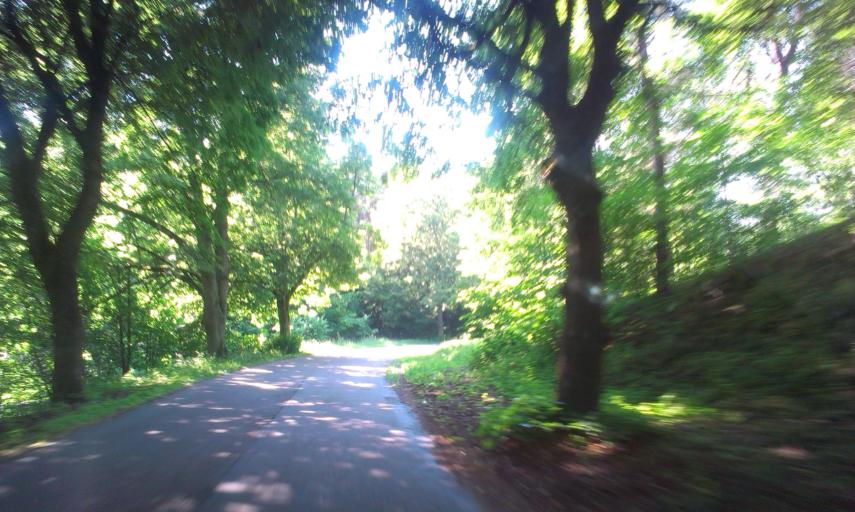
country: PL
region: West Pomeranian Voivodeship
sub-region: Powiat szczecinecki
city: Lubowo
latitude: 53.6271
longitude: 16.3461
